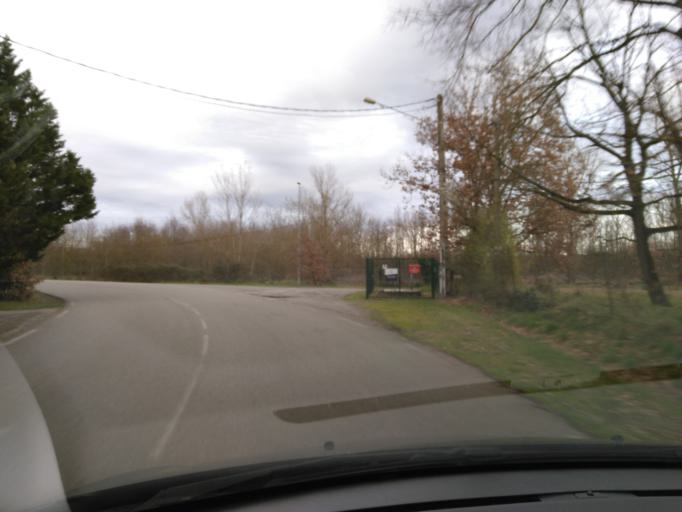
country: FR
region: Midi-Pyrenees
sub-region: Departement de la Haute-Garonne
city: Frouzins
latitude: 43.5012
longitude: 1.3415
